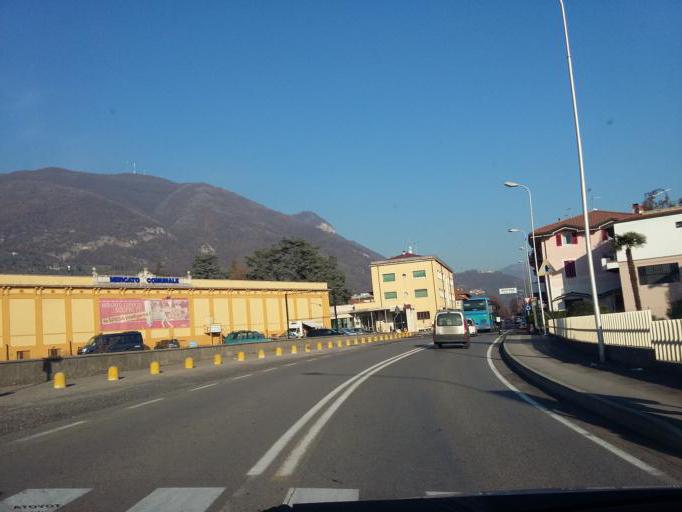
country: IT
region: Lombardy
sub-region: Provincia di Brescia
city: Gavardo-Sopraponte
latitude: 45.5946
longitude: 10.4429
